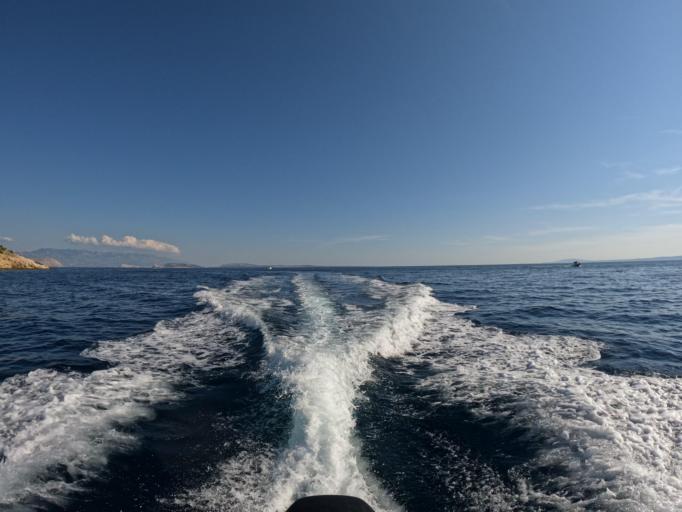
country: HR
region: Primorsko-Goranska
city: Punat
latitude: 44.9652
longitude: 14.6480
